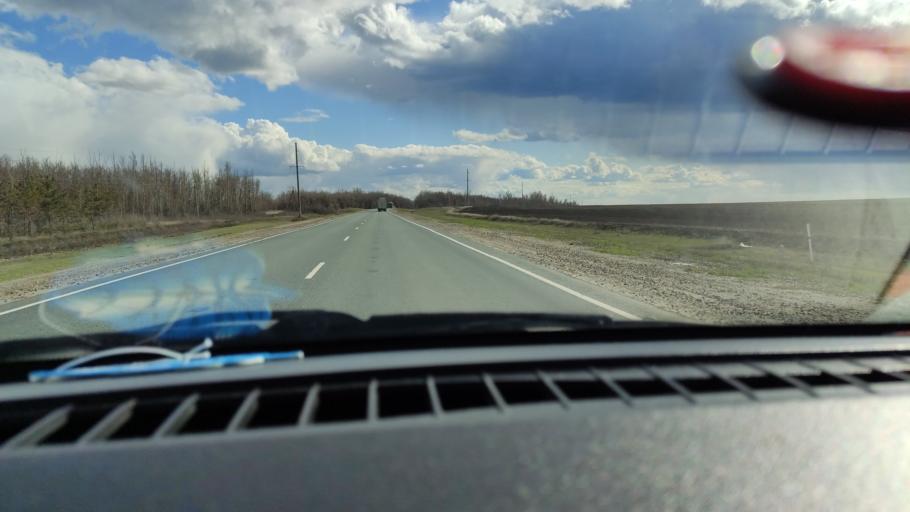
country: RU
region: Saratov
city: Alekseyevka
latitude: 52.2733
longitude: 47.9303
